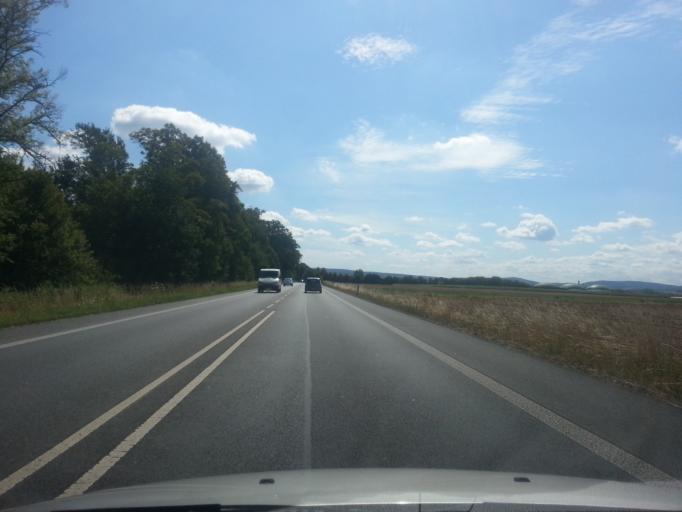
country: DE
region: Hesse
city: Dieburg
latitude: 49.8896
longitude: 8.8664
